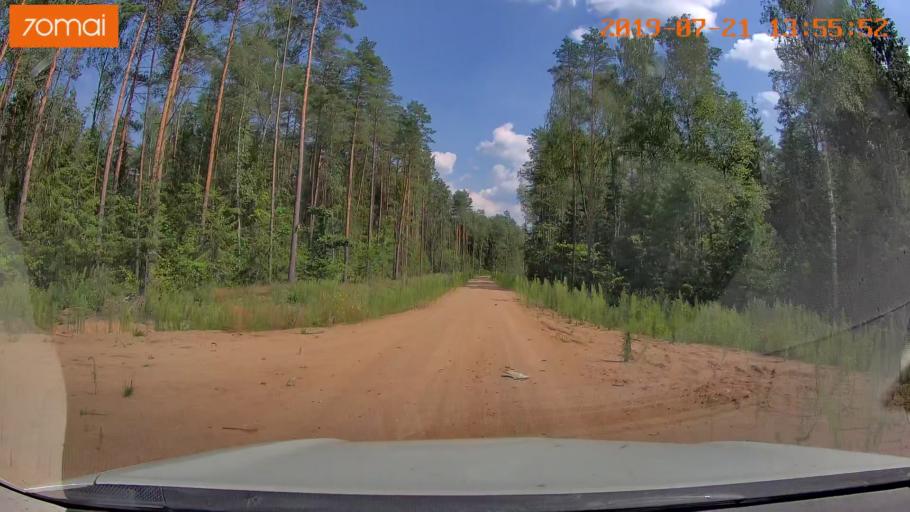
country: BY
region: Grodnenskaya
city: Lyubcha
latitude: 53.7813
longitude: 26.0942
